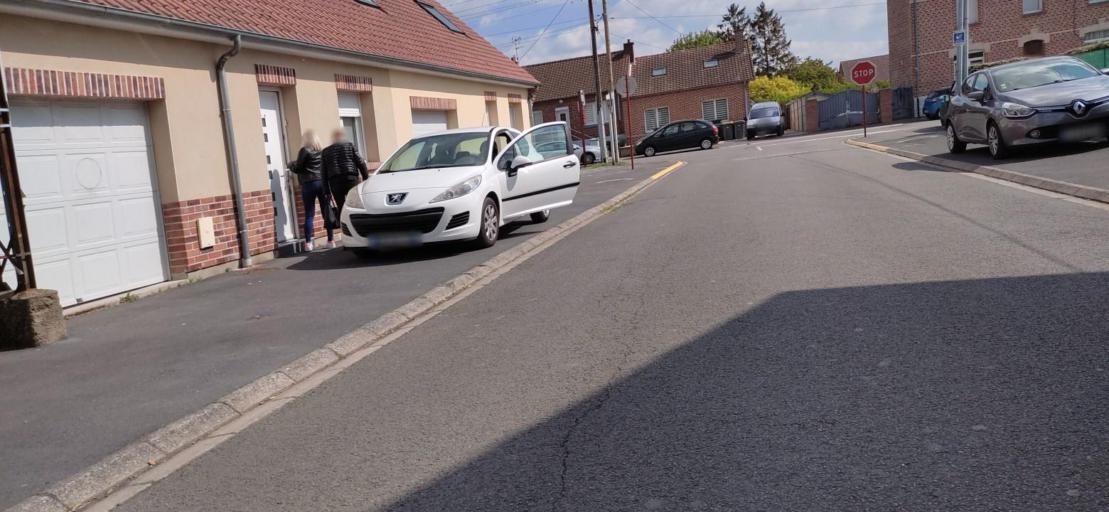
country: FR
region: Nord-Pas-de-Calais
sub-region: Departement du Pas-de-Calais
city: Biache-Saint-Vaast
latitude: 50.3133
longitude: 2.9429
